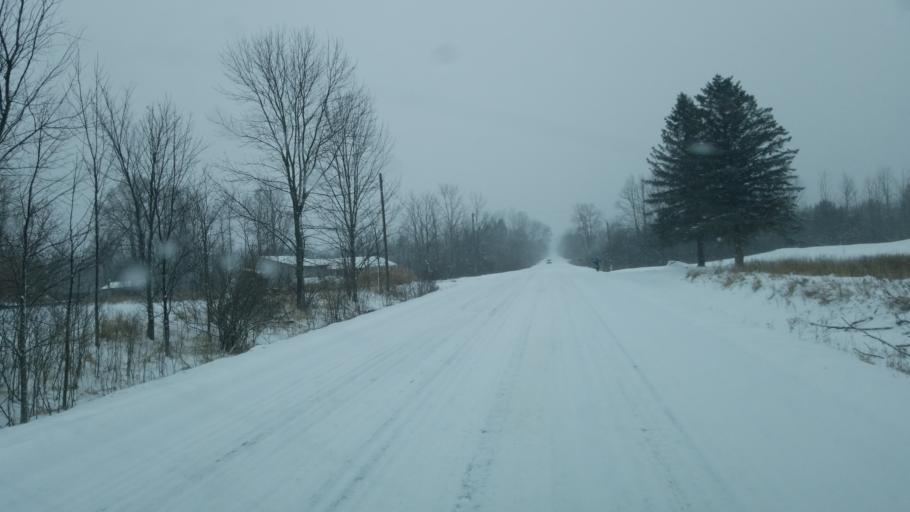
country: US
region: Michigan
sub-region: Mecosta County
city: Canadian Lakes
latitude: 43.5767
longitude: -85.4199
